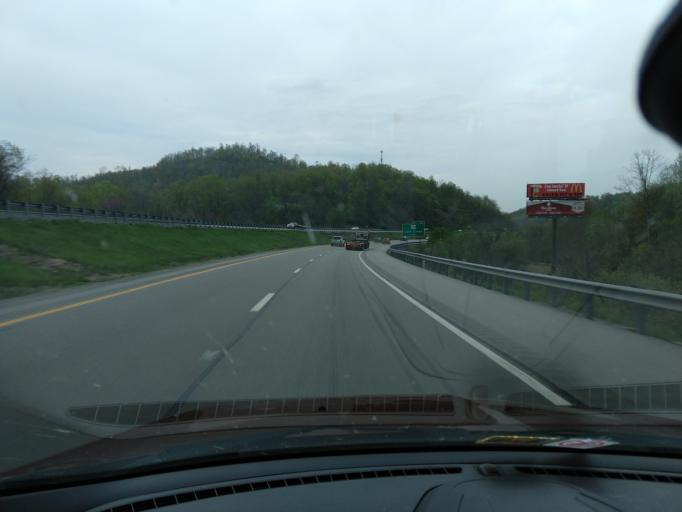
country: US
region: West Virginia
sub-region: Harrison County
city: Stonewood
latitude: 39.1468
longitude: -80.3628
